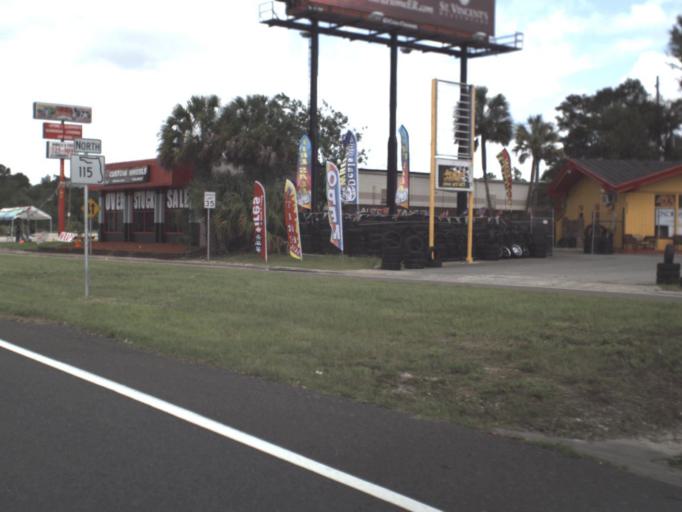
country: US
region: Florida
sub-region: Duval County
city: Jacksonville
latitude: 30.3264
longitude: -81.5668
